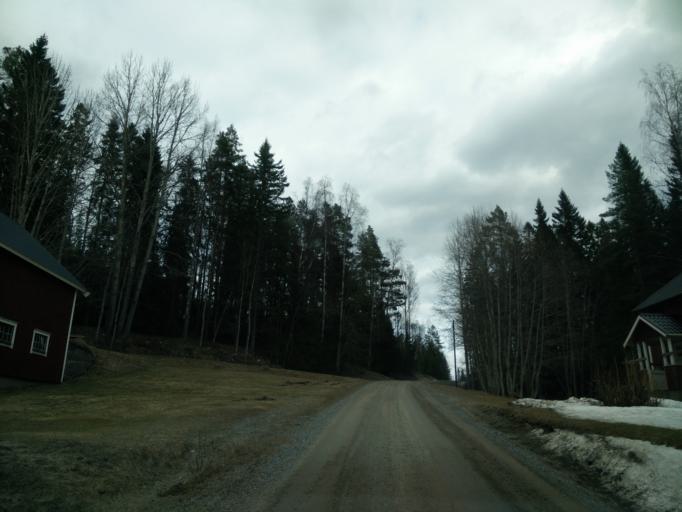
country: SE
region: Vaesternorrland
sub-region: Haernoesands Kommun
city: Haernoesand
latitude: 62.7353
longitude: 18.0372
